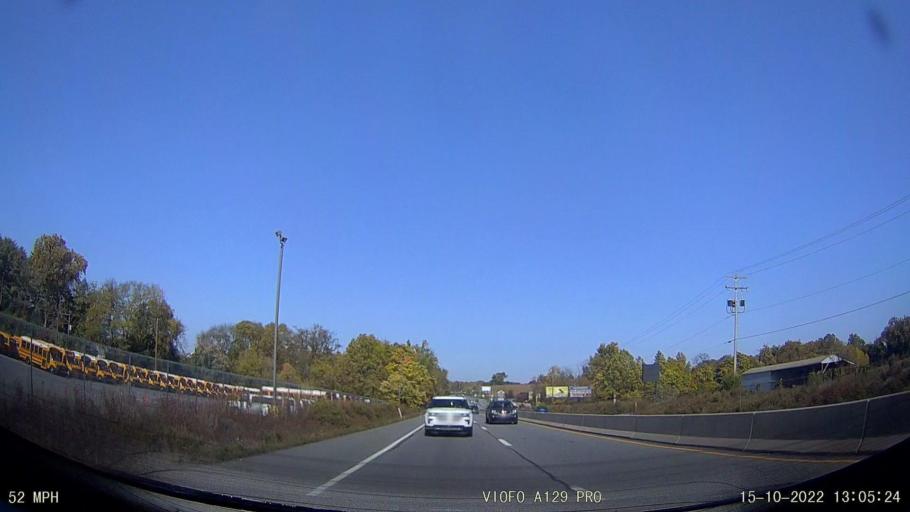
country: US
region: Pennsylvania
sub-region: Berks County
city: Temple
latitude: 40.4246
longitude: -75.9386
